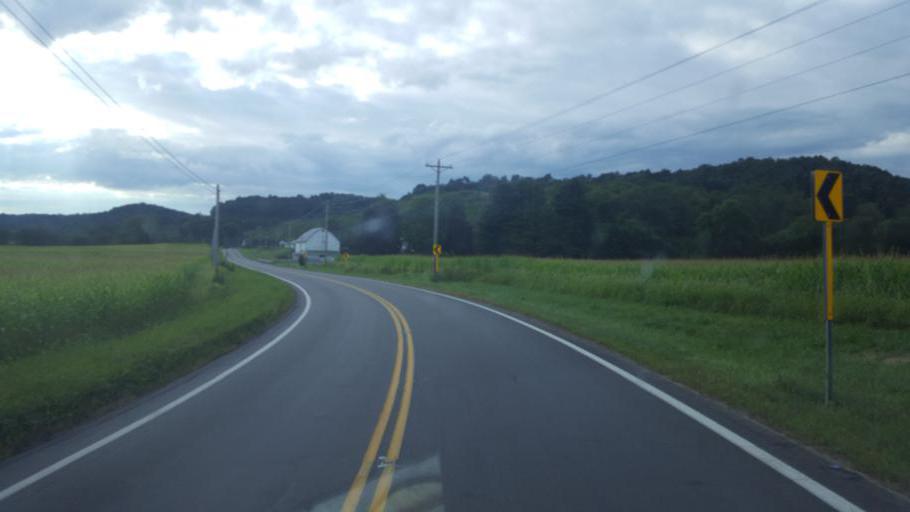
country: US
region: Ohio
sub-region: Holmes County
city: Millersburg
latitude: 40.4819
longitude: -82.0319
